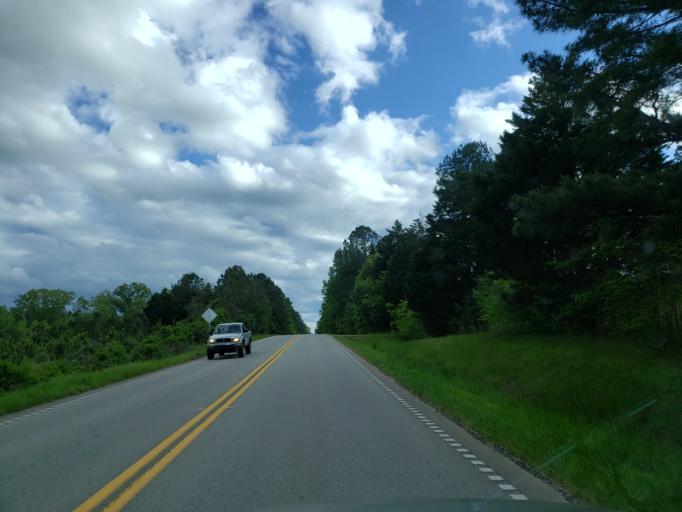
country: US
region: Georgia
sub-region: Haralson County
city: Tallapoosa
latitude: 33.8482
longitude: -85.2920
